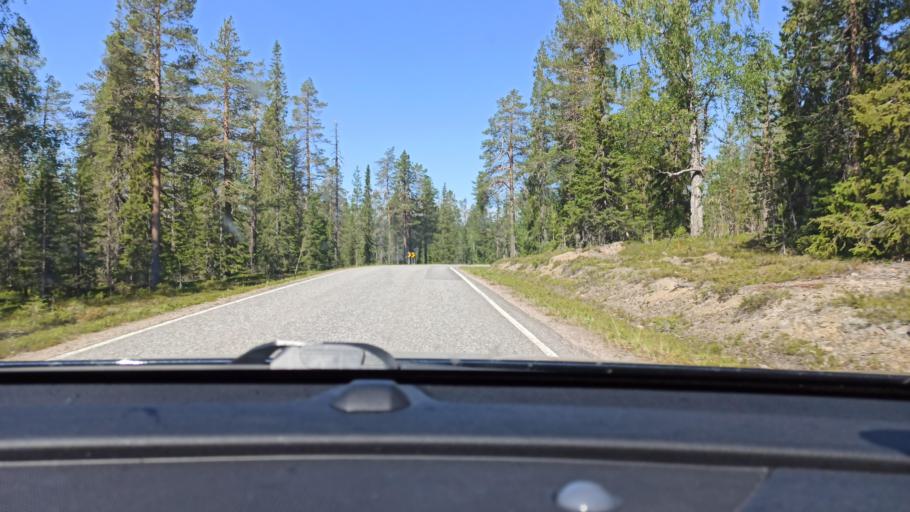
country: FI
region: Lapland
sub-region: Tunturi-Lappi
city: Kolari
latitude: 67.6703
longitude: 24.1520
